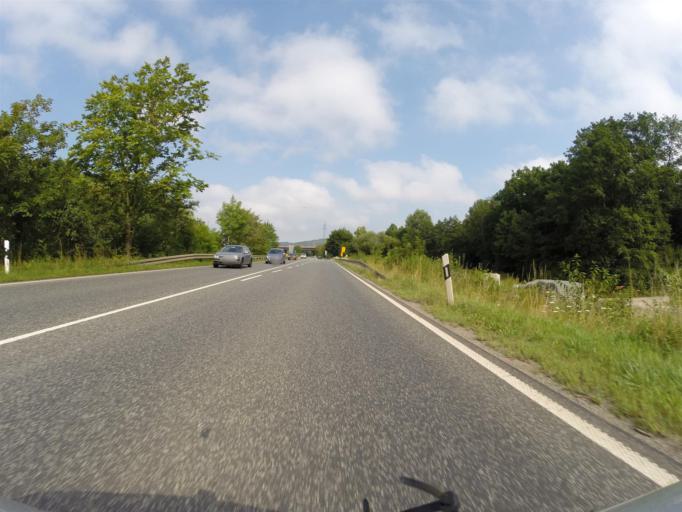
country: DE
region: Hesse
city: Waldkappel
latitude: 51.1529
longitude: 9.8715
